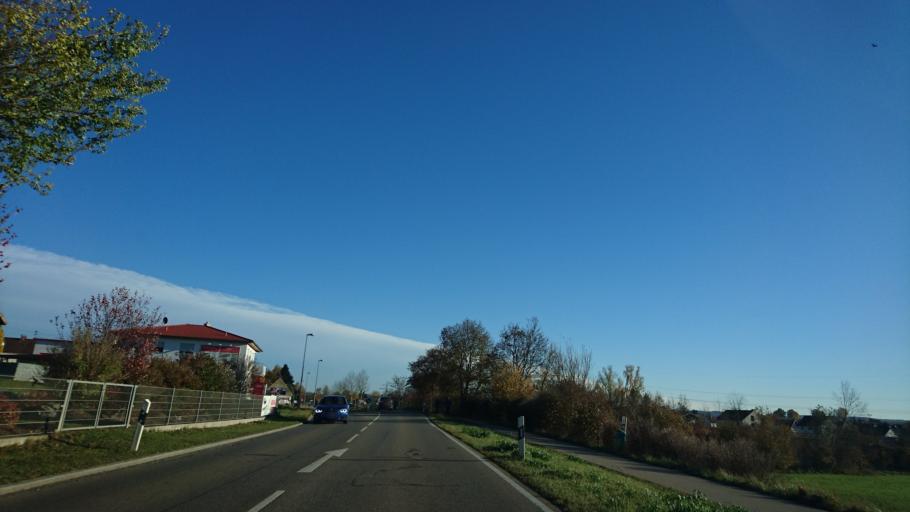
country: DE
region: Bavaria
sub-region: Swabia
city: Dinkelscherben
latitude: 48.3503
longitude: 10.5813
